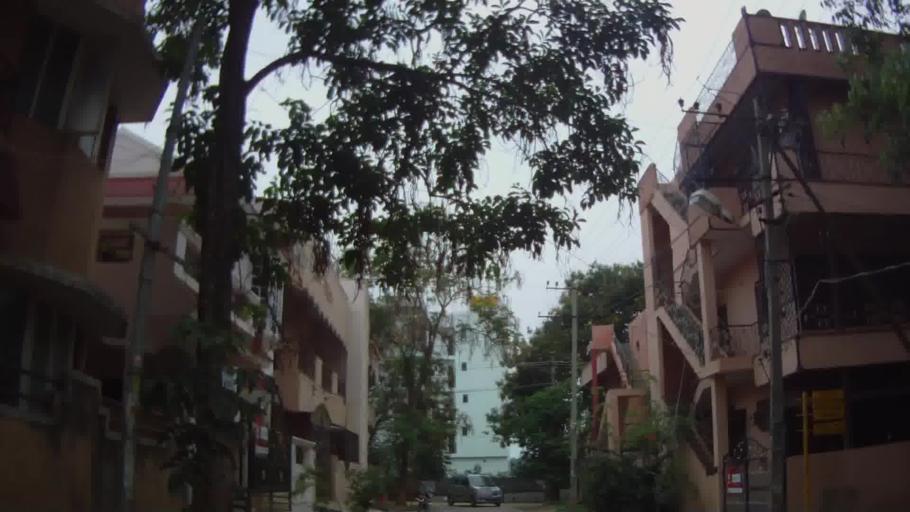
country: IN
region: Karnataka
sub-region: Bangalore Urban
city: Bangalore
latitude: 12.9609
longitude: 77.7120
